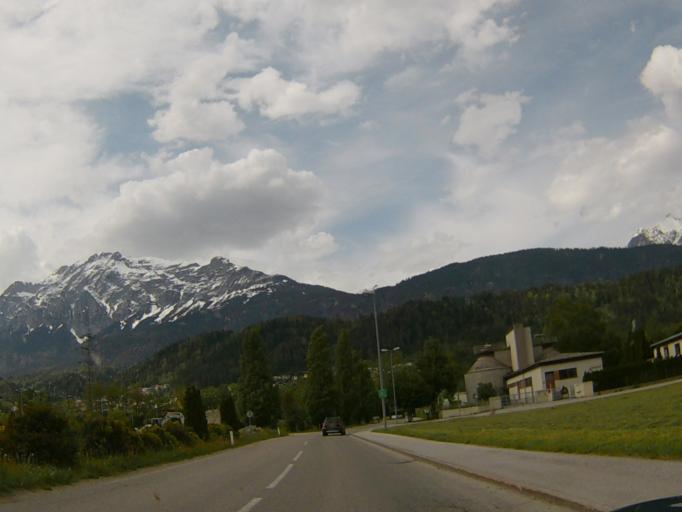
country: AT
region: Tyrol
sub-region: Politischer Bezirk Innsbruck Land
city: Wattenberg
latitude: 47.2967
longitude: 11.6046
